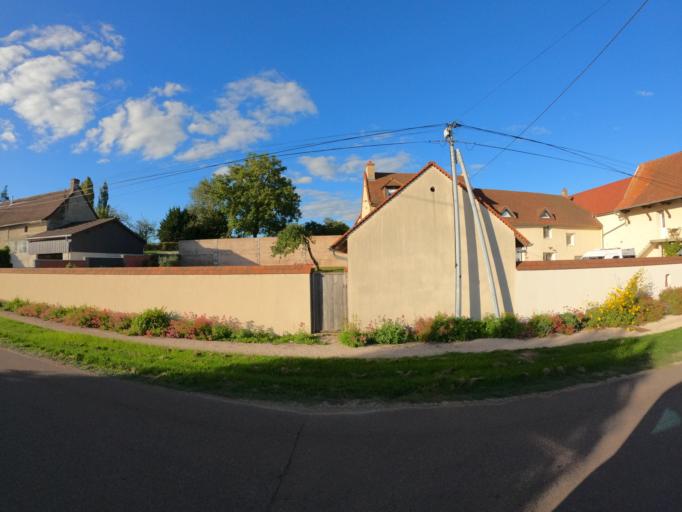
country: FR
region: Bourgogne
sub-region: Departement de Saone-et-Loire
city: Ecuisses
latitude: 46.7375
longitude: 4.5553
